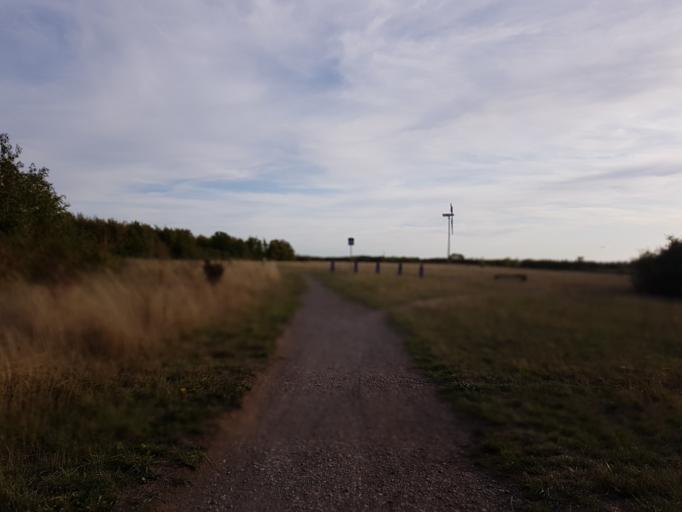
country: DE
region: Lower Saxony
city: Laatzen
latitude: 52.3306
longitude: 9.8359
